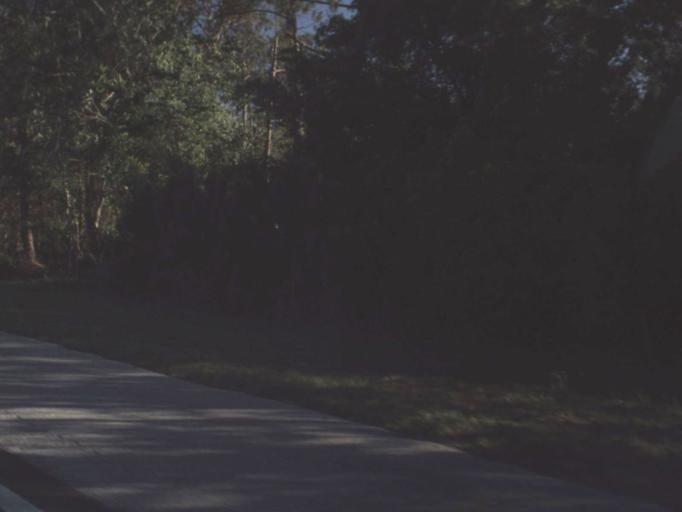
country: US
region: Florida
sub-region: Flagler County
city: Palm Coast
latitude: 29.5659
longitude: -81.2267
